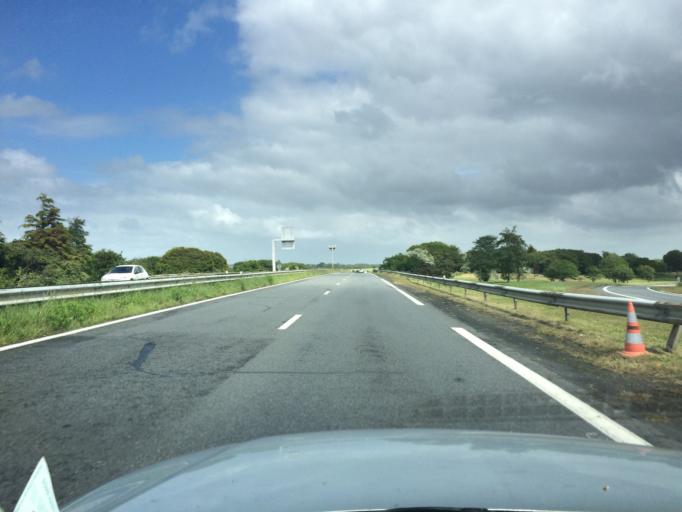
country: FR
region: Brittany
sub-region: Departement du Finistere
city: Gouesnou
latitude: 48.4334
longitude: -4.4452
